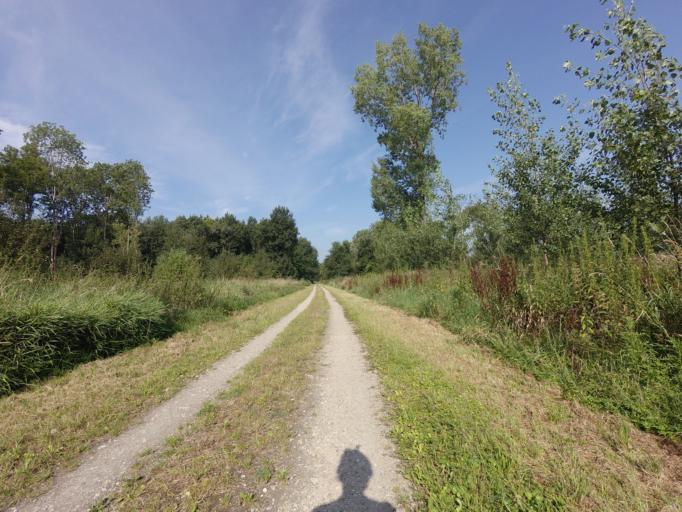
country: NL
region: North Holland
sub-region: Gemeente Huizen
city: Huizen
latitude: 52.3224
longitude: 5.3013
